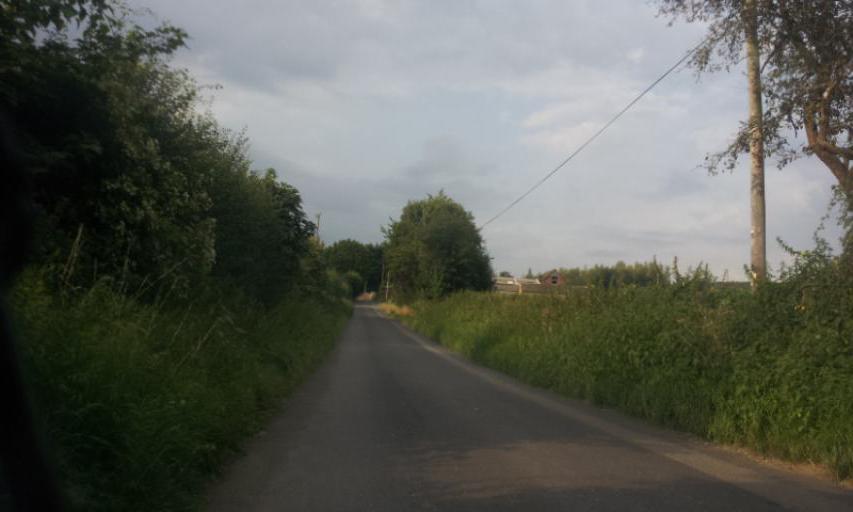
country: GB
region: England
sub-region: Kent
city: Yalding
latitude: 51.2341
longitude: 0.4235
